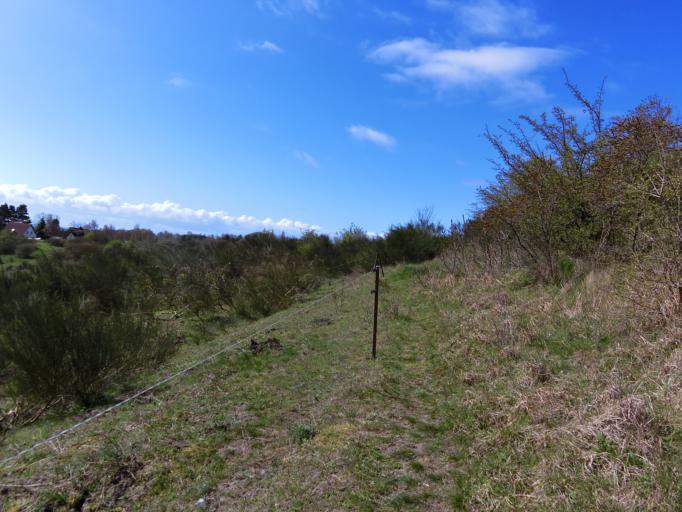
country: DE
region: Mecklenburg-Vorpommern
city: Hiddensee
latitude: 54.5909
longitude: 13.1107
